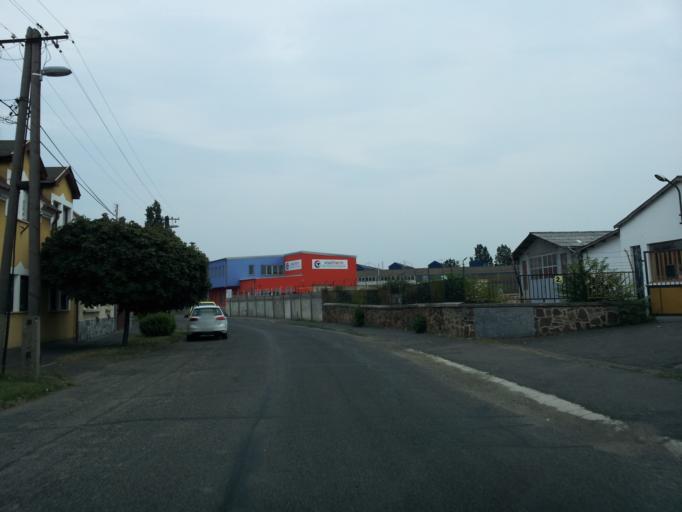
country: HU
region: Vas
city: Szombathely
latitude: 47.2350
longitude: 16.6374
